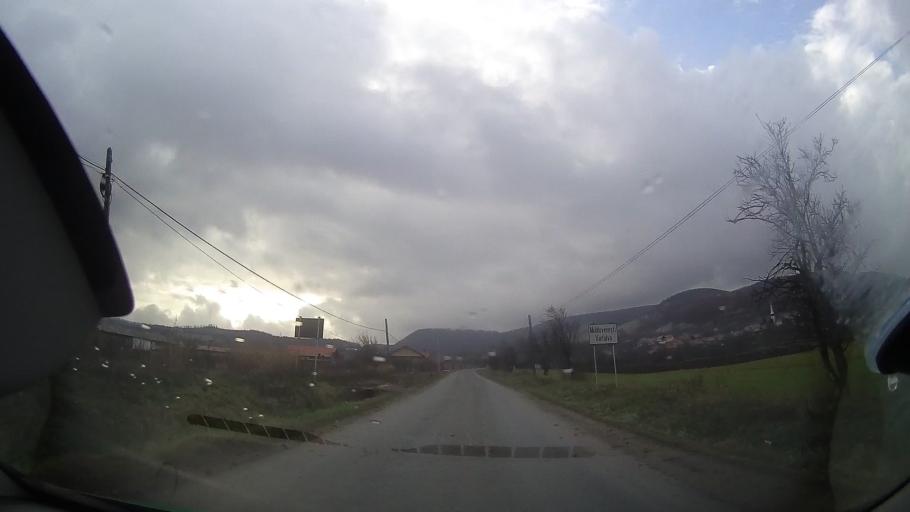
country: RO
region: Cluj
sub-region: Comuna Moldovenesti
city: Moldovenesti
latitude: 46.5047
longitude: 23.6670
